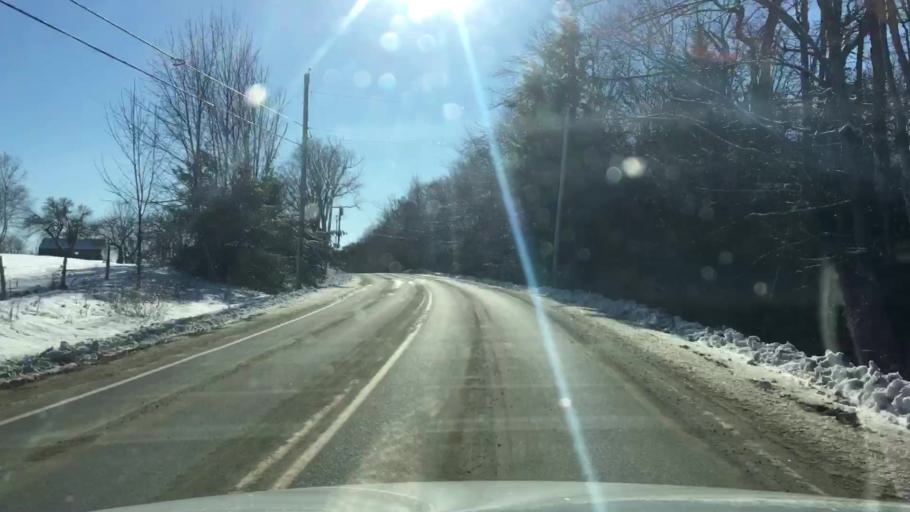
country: US
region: Maine
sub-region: Kennebec County
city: Readfield
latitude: 44.3833
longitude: -69.9794
